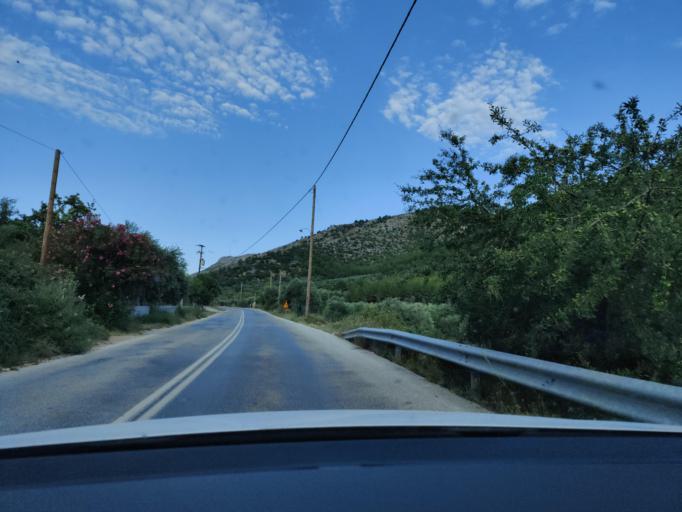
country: GR
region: East Macedonia and Thrace
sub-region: Nomos Kavalas
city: Limenaria
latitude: 40.6133
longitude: 24.6323
